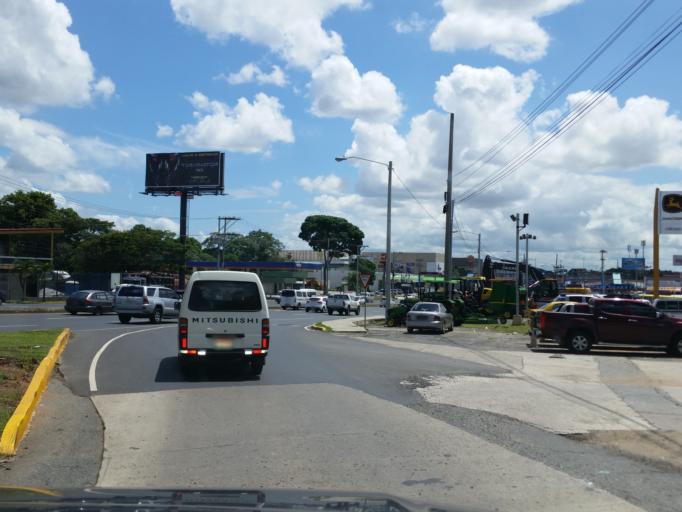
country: PA
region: Panama
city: San Miguelito
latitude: 9.0494
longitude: -79.4571
